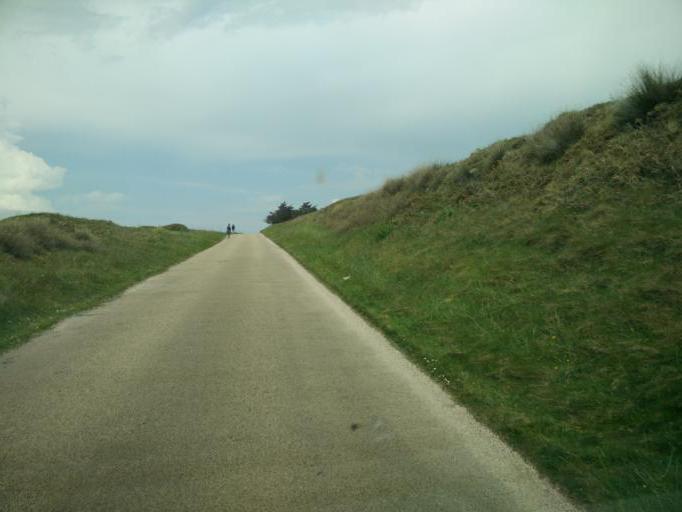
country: FR
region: Brittany
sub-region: Departement du Finistere
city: Camaret-sur-Mer
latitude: 48.2790
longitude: -4.6116
